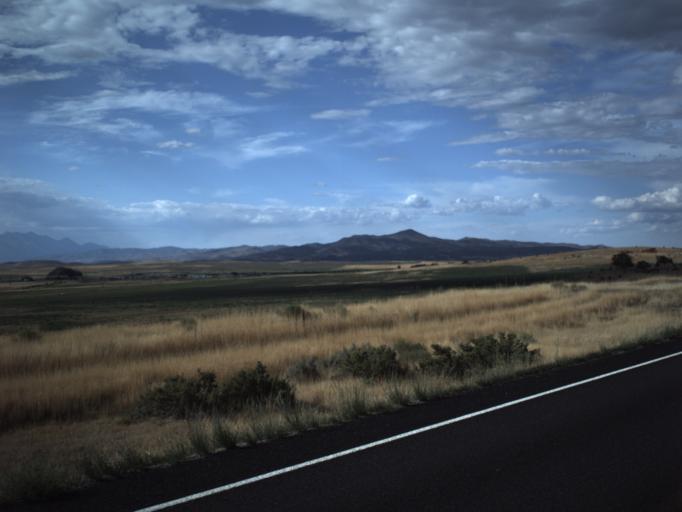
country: US
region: Utah
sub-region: Sanpete County
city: Moroni
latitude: 39.4713
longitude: -111.5297
